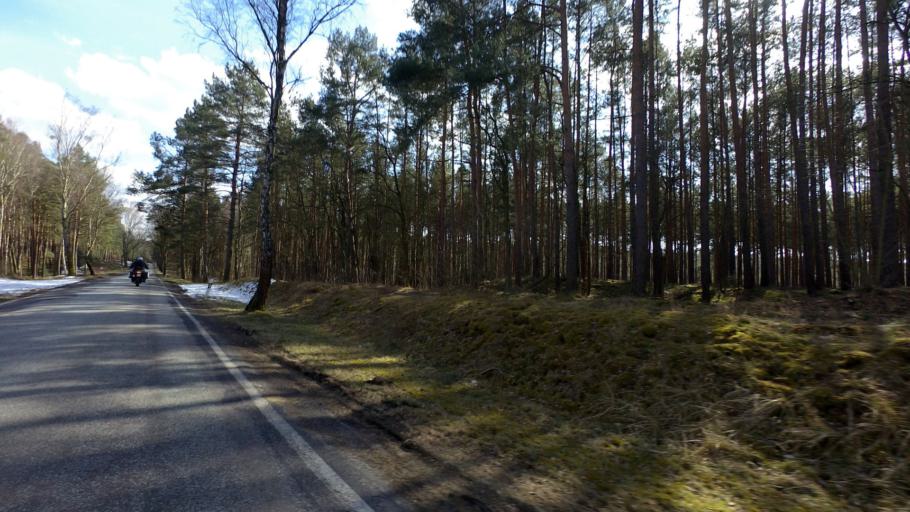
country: DE
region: Brandenburg
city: Biesenthal
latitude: 52.7829
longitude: 13.6109
